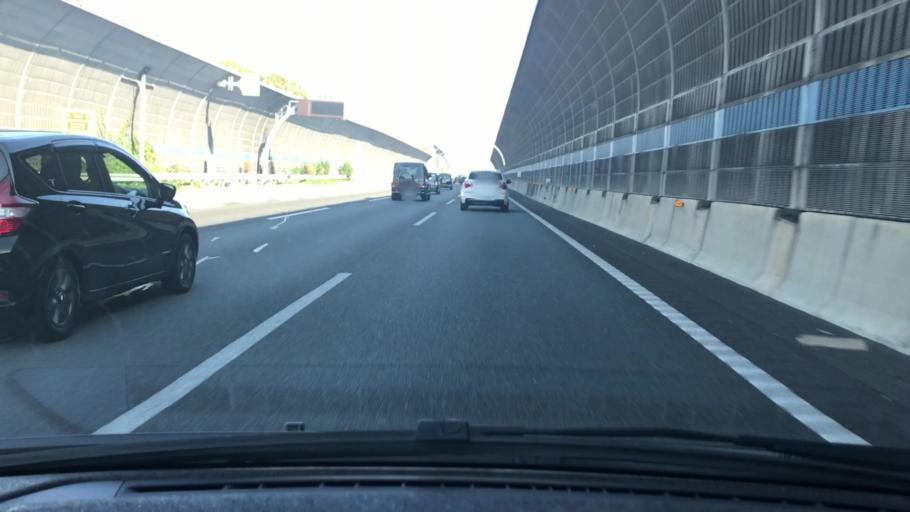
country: JP
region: Osaka
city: Ibaraki
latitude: 34.8112
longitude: 135.5459
